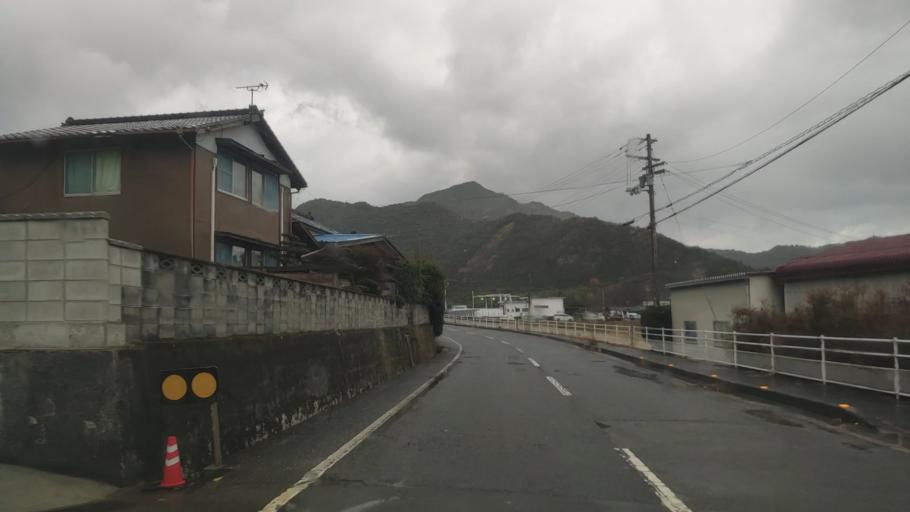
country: JP
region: Tokushima
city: Kamojimacho-jogejima
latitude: 34.2095
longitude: 134.3332
